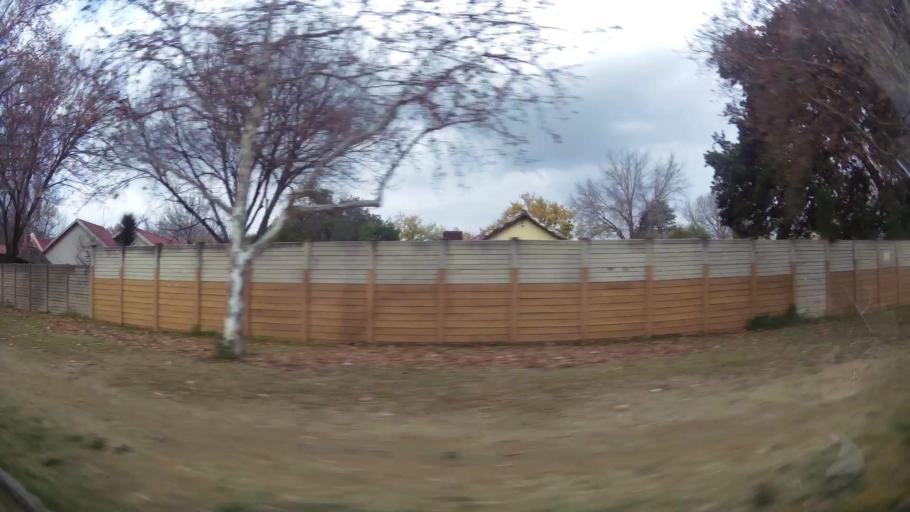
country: ZA
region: Orange Free State
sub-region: Fezile Dabi District Municipality
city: Sasolburg
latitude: -26.8069
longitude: 27.8293
